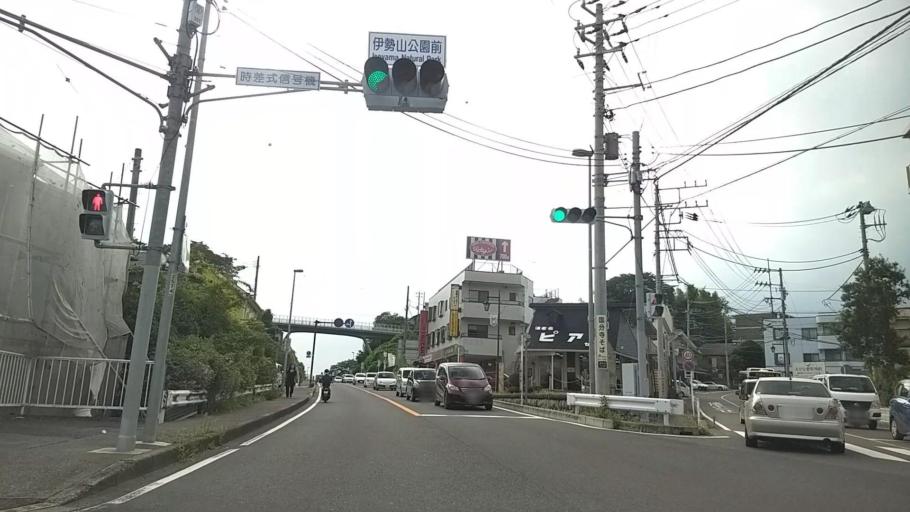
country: JP
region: Kanagawa
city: Zama
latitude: 35.4529
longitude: 139.4021
